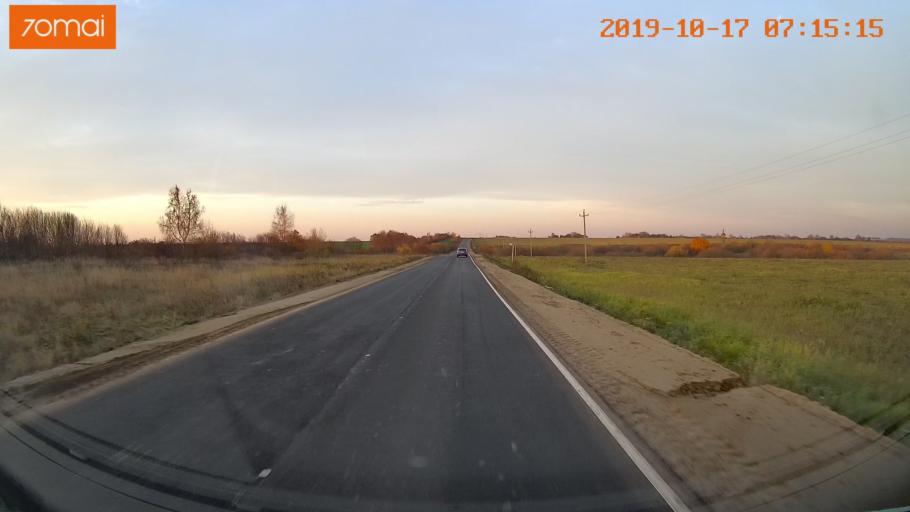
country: RU
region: Vladimir
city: Suzdal'
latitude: 56.3825
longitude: 40.2714
